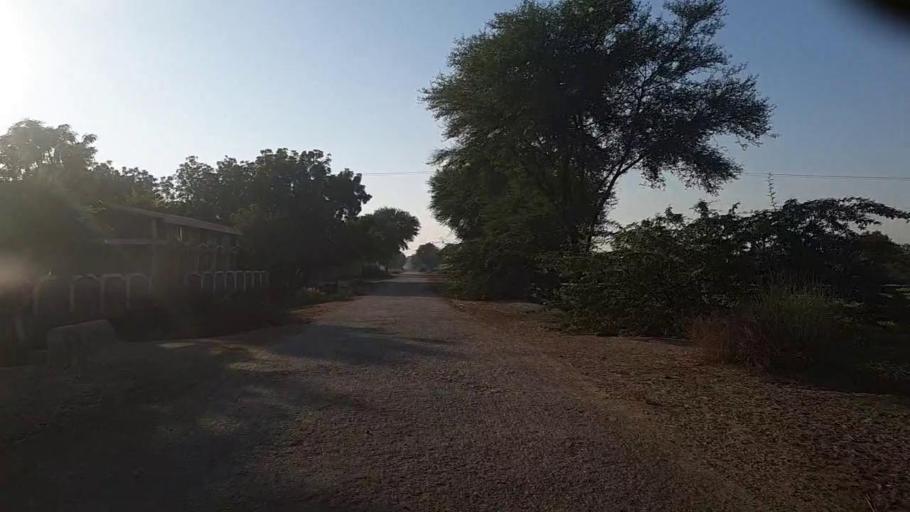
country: PK
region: Sindh
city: Pad Idan
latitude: 26.7342
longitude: 68.3393
